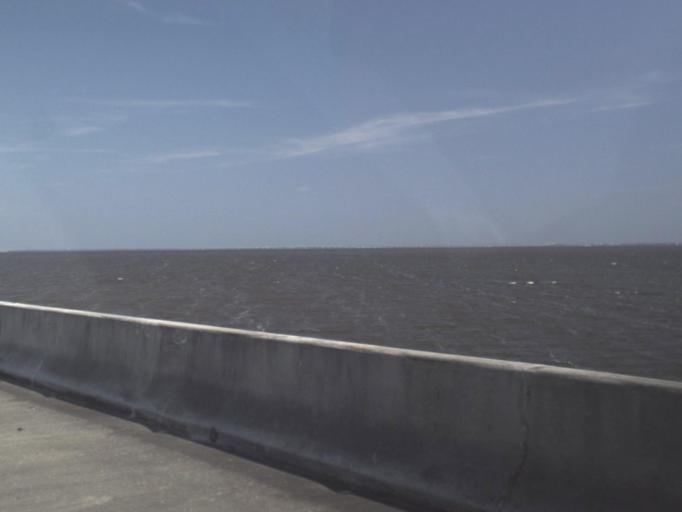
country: US
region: Florida
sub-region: Franklin County
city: Apalachicola
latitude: 29.7299
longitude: -84.9411
